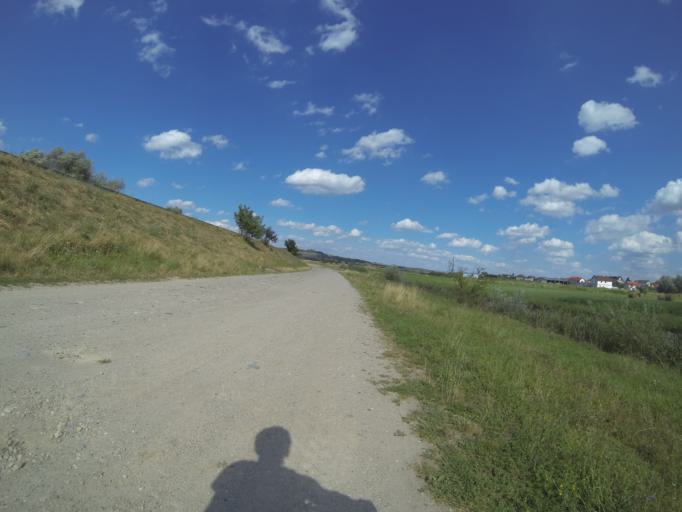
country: RO
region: Brasov
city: Fogarasch
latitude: 45.8482
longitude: 24.9821
